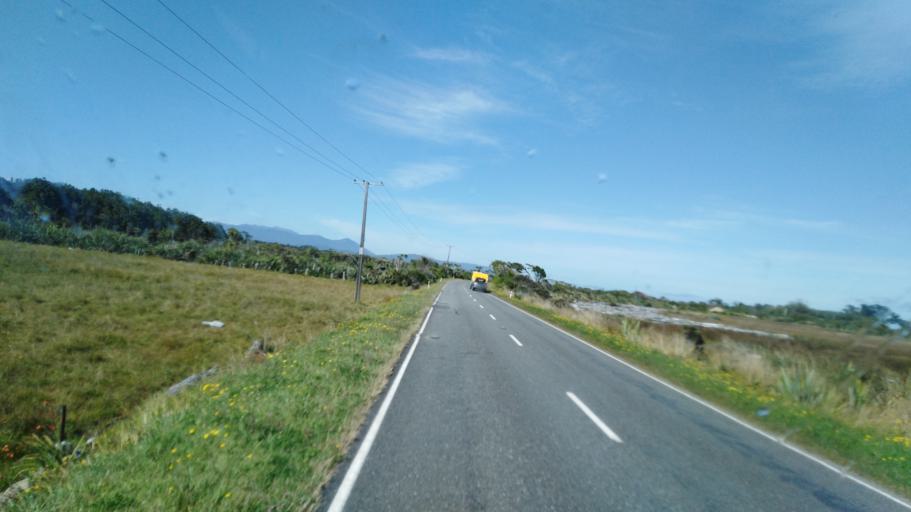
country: NZ
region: West Coast
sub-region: Buller District
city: Westport
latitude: -41.2873
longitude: 172.1030
